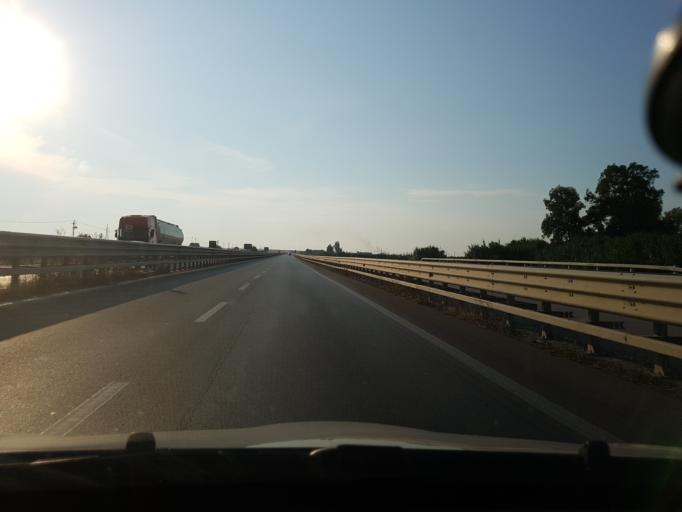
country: IT
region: Apulia
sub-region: Provincia di Foggia
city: Orta Nova
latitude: 41.3354
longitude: 15.7557
